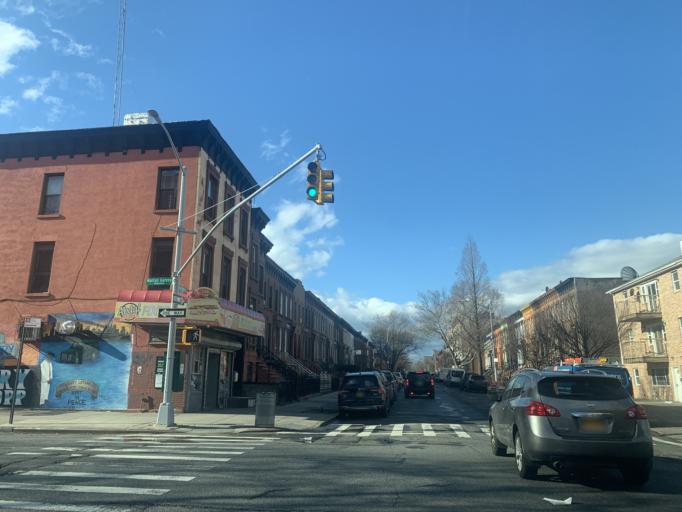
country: US
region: New York
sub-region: Kings County
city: Brooklyn
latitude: 40.6905
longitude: -73.9394
